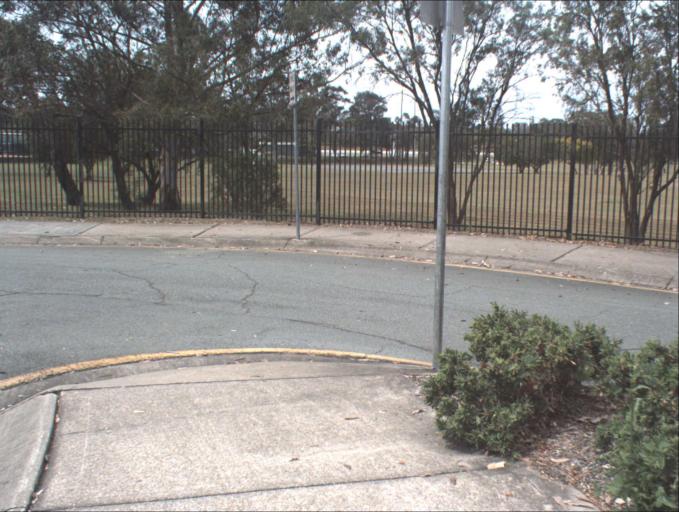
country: AU
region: Queensland
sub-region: Logan
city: Beenleigh
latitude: -27.7140
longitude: 153.2039
